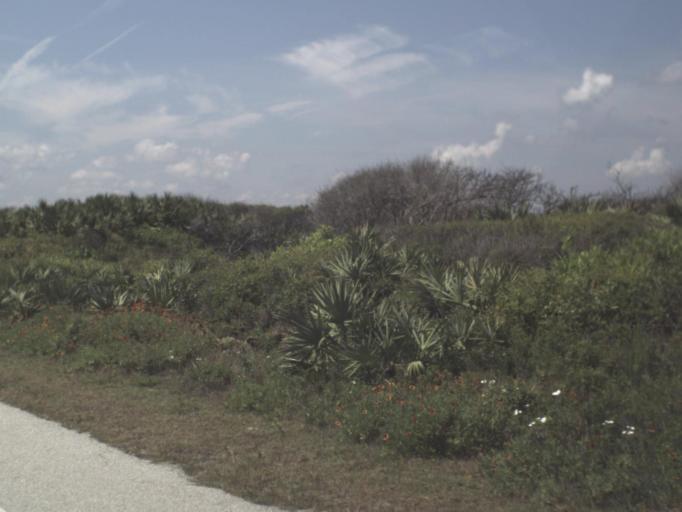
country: US
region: Florida
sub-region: Saint Johns County
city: Palm Valley
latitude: 30.1091
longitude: -81.3438
